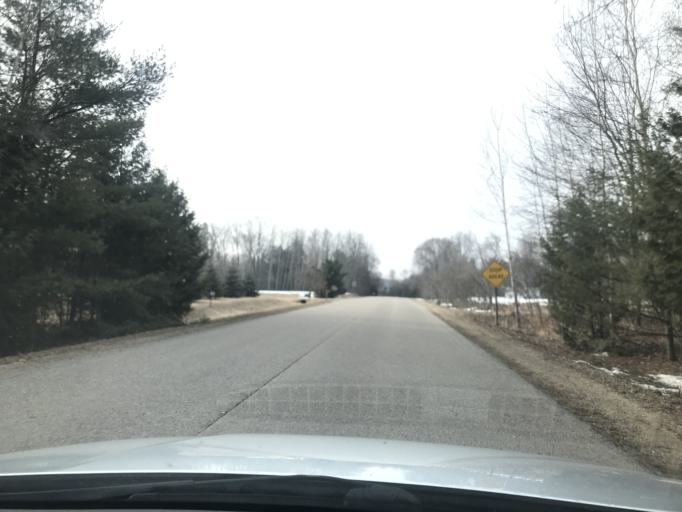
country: US
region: Wisconsin
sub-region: Oconto County
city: Oconto Falls
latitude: 44.8529
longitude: -88.1472
